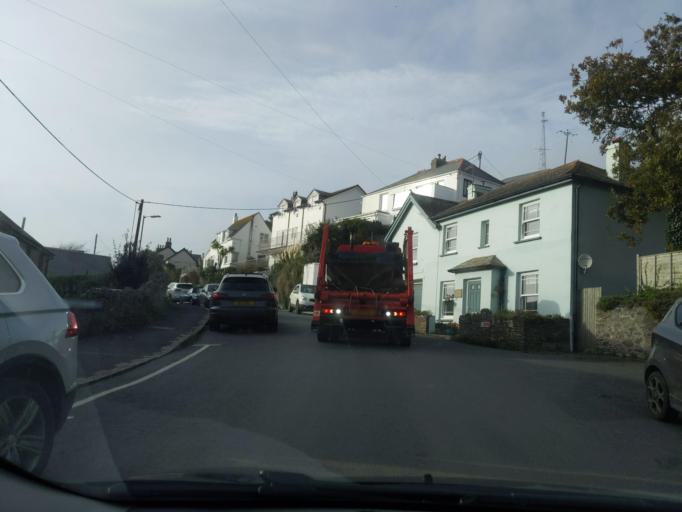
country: GB
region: England
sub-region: Cornwall
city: Looe
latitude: 50.3622
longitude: -4.3712
